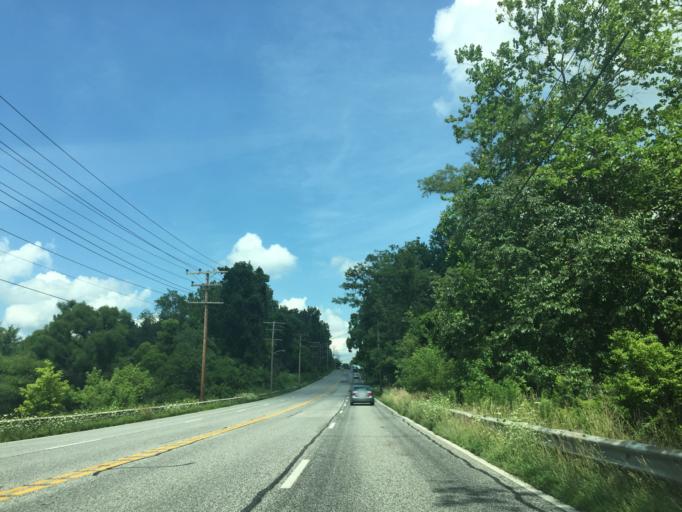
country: US
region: Maryland
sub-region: Baltimore County
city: Kingsville
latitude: 39.4407
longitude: -76.4257
